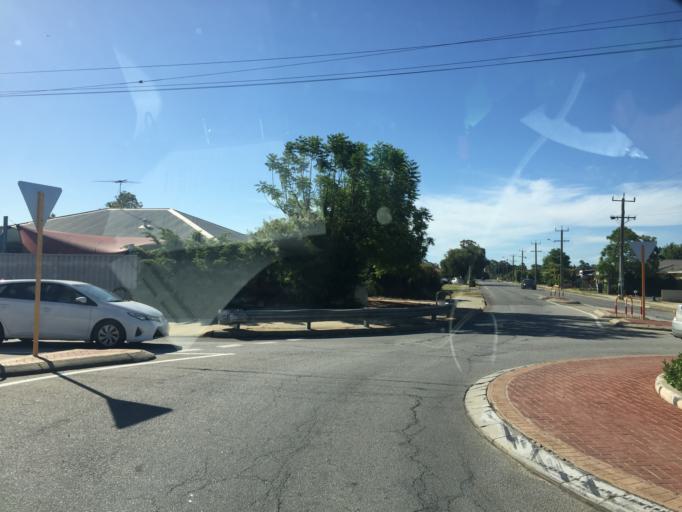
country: AU
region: Western Australia
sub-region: Gosnells
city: Kenwick
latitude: -32.0212
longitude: 115.9631
